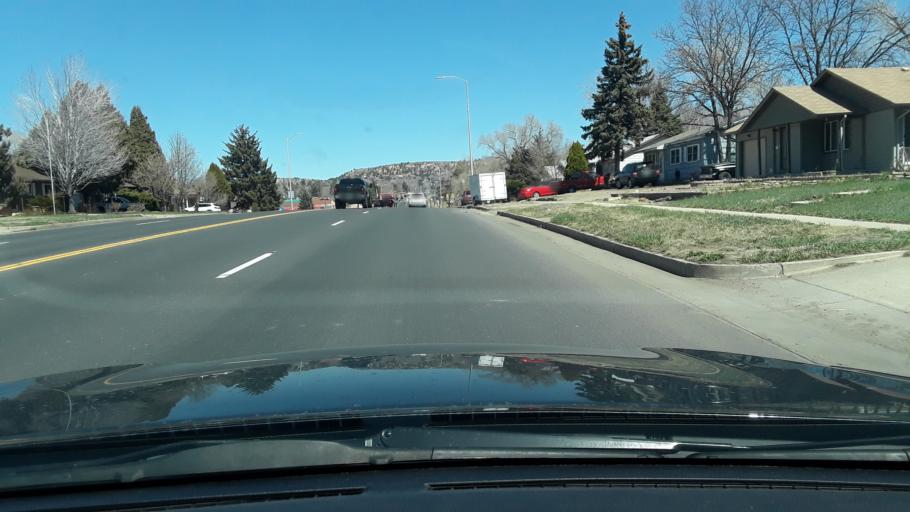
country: US
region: Colorado
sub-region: El Paso County
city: Colorado Springs
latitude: 38.8520
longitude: -104.7757
